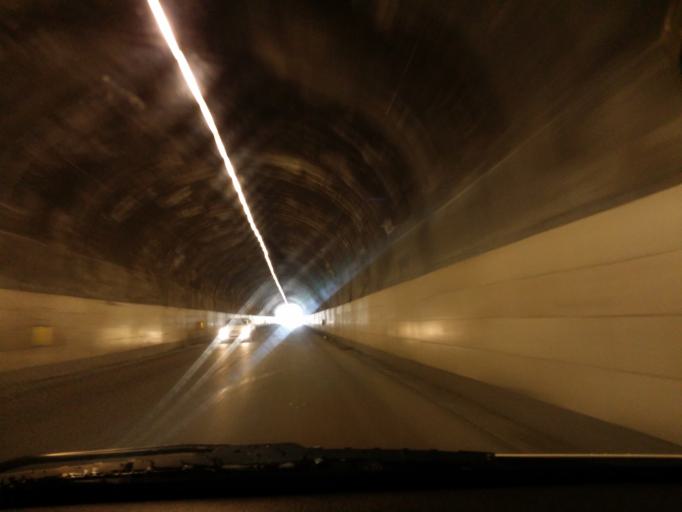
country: IR
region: Alborz
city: Karaj
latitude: 35.9797
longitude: 51.0930
